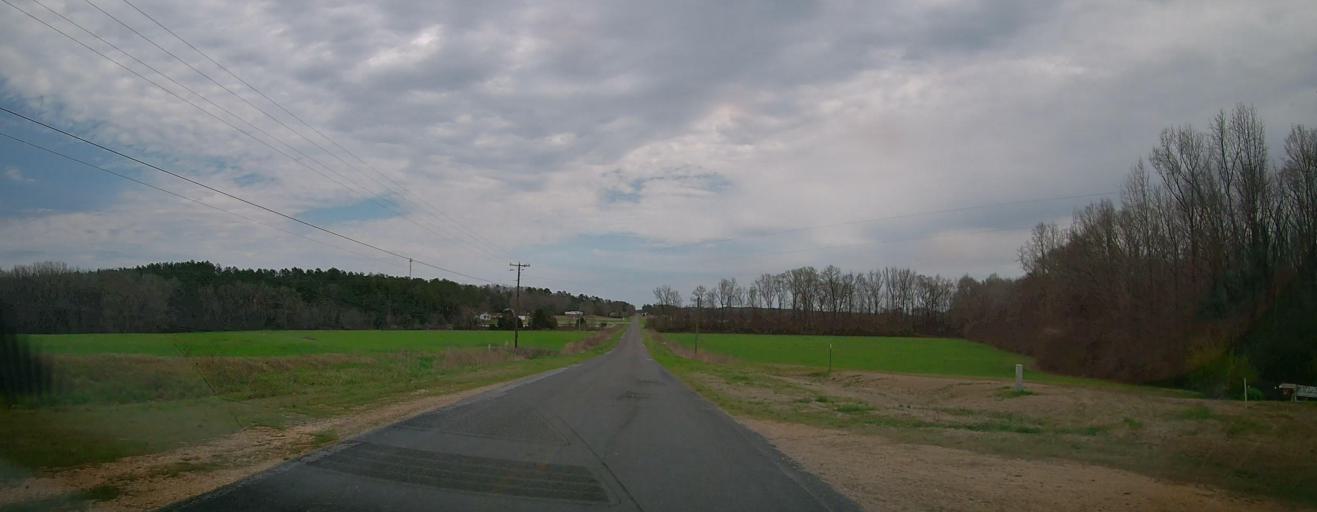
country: US
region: Alabama
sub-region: Marion County
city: Hamilton
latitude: 34.1965
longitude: -88.1622
